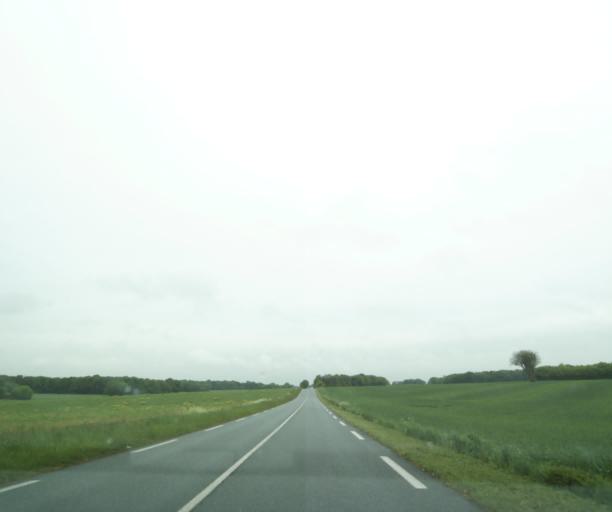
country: FR
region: Poitou-Charentes
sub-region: Departement de la Charente-Maritime
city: Nieul-les-Saintes
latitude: 45.7449
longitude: -0.7183
